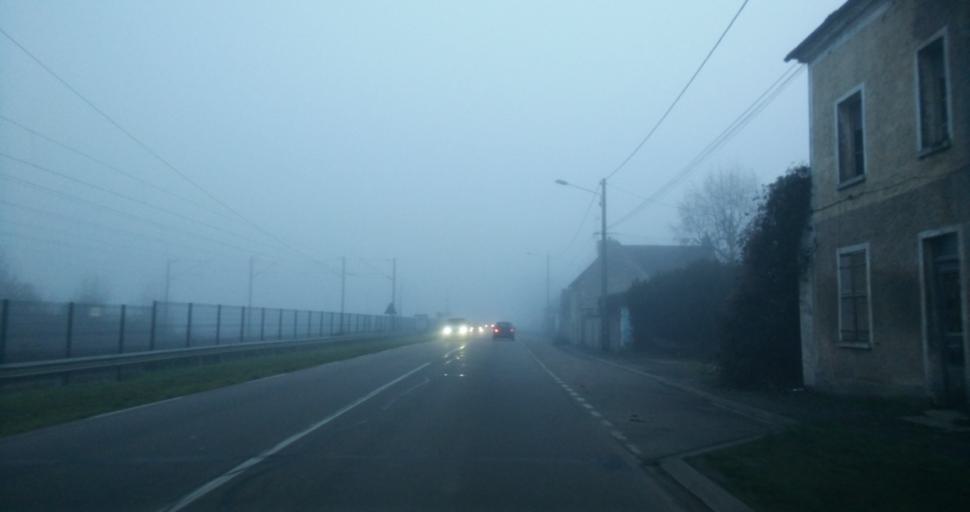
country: FR
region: Haute-Normandie
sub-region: Departement de l'Eure
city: Saint-Just
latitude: 49.1255
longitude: 1.4360
